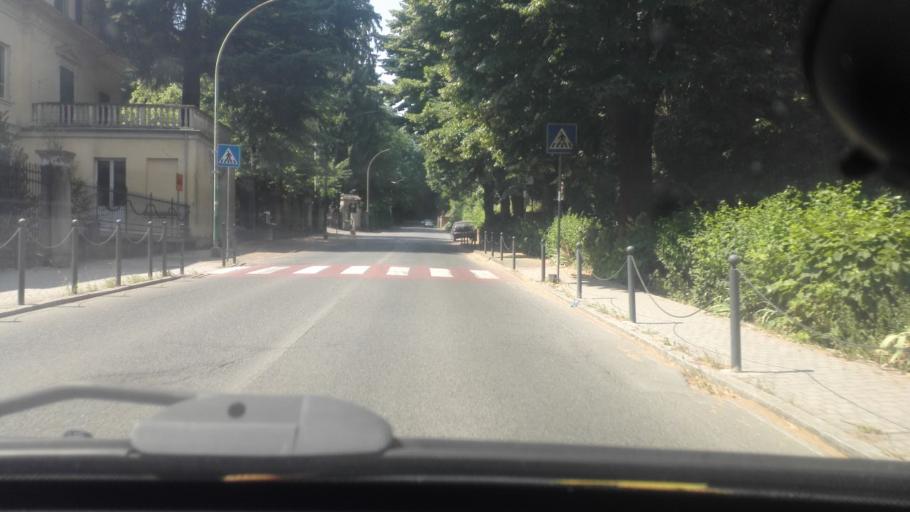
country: IT
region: Piedmont
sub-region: Provincia di Alessandria
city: Novi Ligure
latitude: 44.7585
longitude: 8.7903
